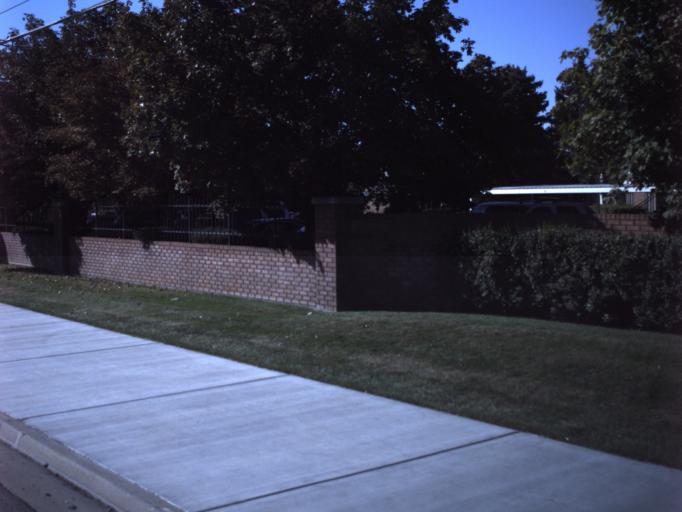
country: US
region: Utah
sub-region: Salt Lake County
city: Centerfield
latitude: 40.6995
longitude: -111.9206
